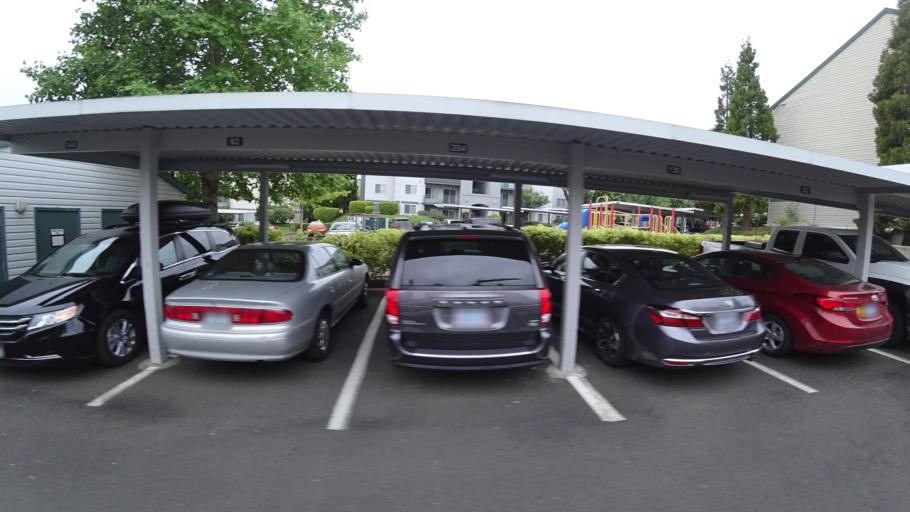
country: US
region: Oregon
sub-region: Washington County
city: Rockcreek
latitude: 45.5213
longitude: -122.8868
